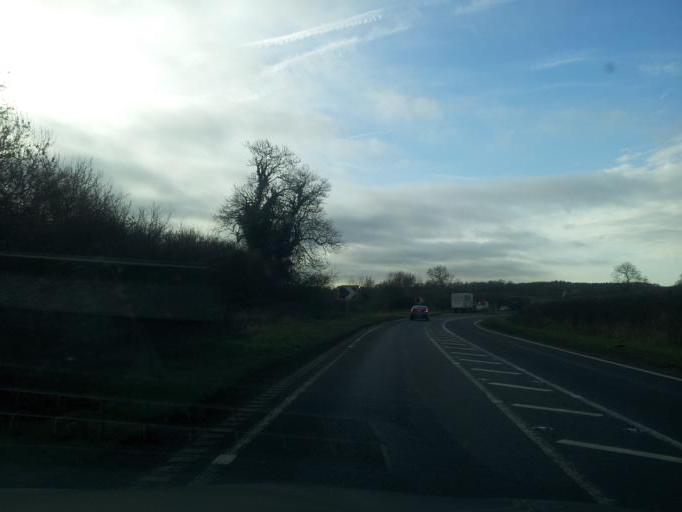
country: GB
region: England
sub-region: District of Rutland
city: Ketton
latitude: 52.5885
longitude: -0.5527
